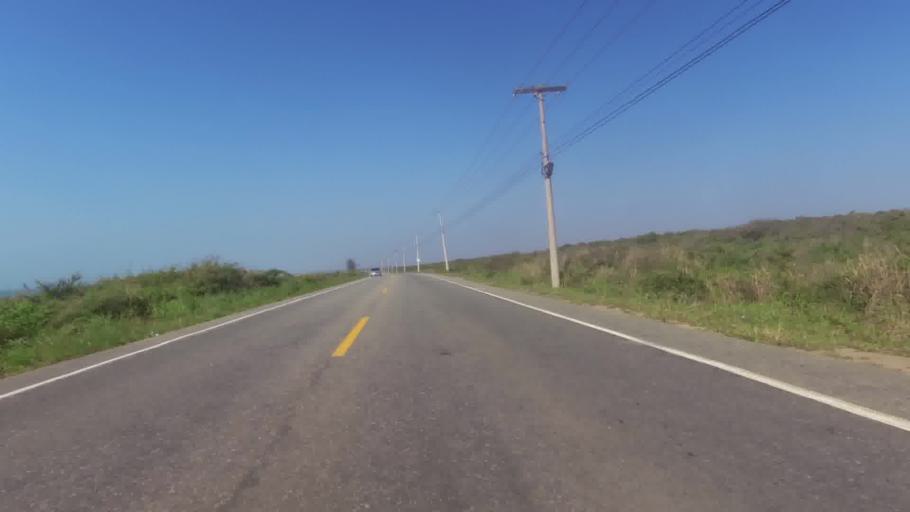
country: BR
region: Espirito Santo
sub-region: Itapemirim
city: Itapemirim
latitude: -20.9438
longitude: -40.8050
